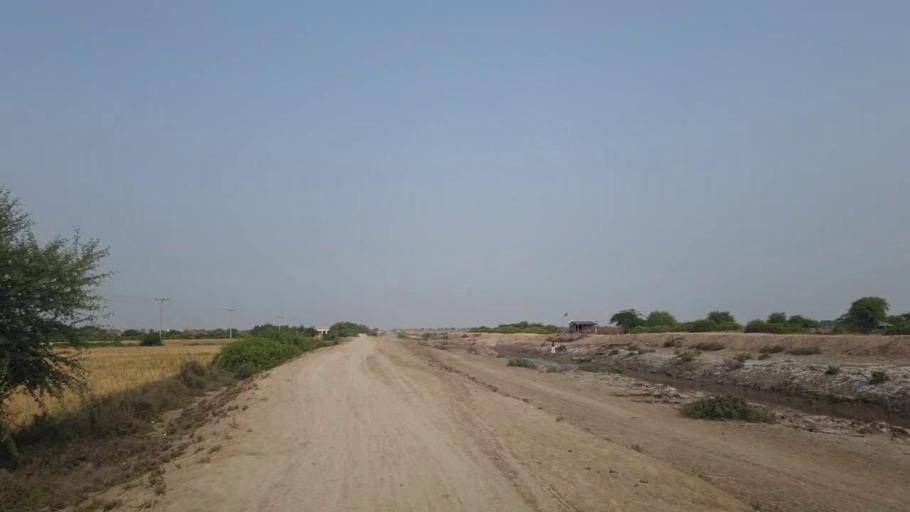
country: PK
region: Sindh
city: Badin
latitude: 24.7139
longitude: 68.7723
